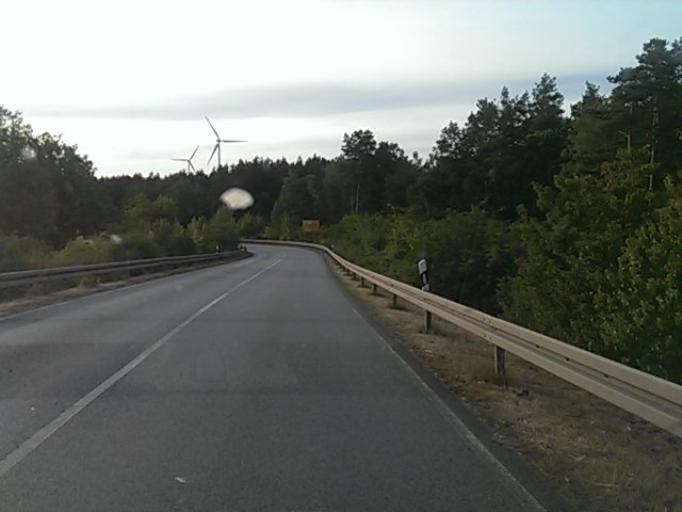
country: DE
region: Brandenburg
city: Ludwigsfelde
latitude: 52.3301
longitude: 13.2746
